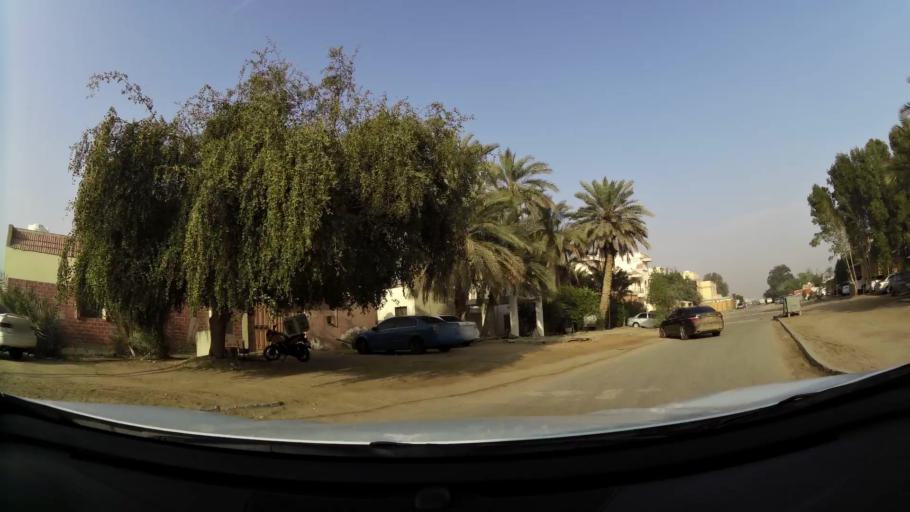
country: AE
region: Abu Dhabi
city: Abu Dhabi
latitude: 24.2925
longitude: 54.6296
